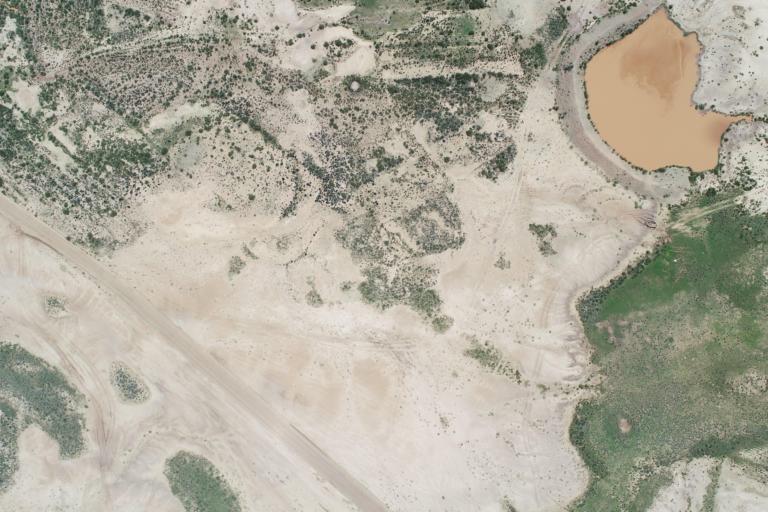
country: BO
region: La Paz
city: Curahuara de Carangas
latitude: -17.3150
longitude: -68.4972
